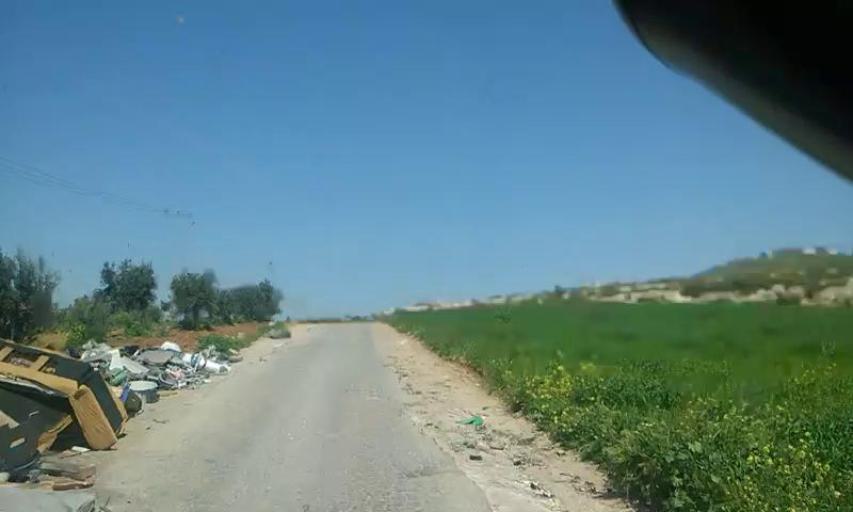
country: PS
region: West Bank
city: Al Majd
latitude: 31.4948
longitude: 34.9605
